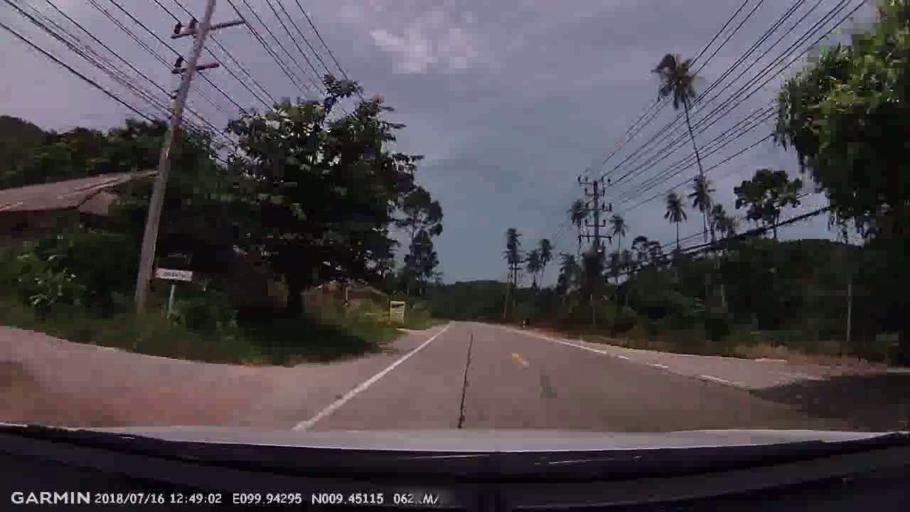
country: TH
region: Surat Thani
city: Ko Samui
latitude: 9.4509
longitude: 99.9430
